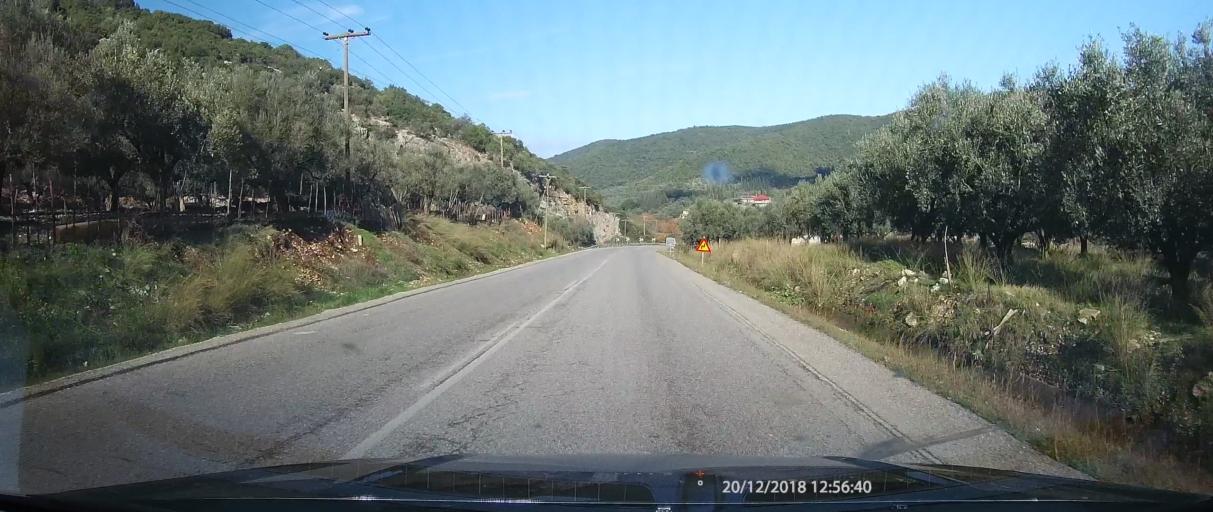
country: GR
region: West Greece
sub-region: Nomos Aitolias kai Akarnanias
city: Pappadhatai
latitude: 38.5135
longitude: 21.3795
